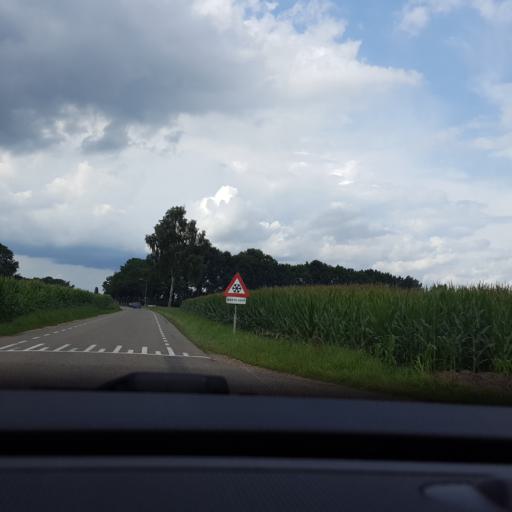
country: NL
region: Gelderland
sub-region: Gemeente Doesburg
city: Doesburg
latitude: 52.0205
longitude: 6.1658
